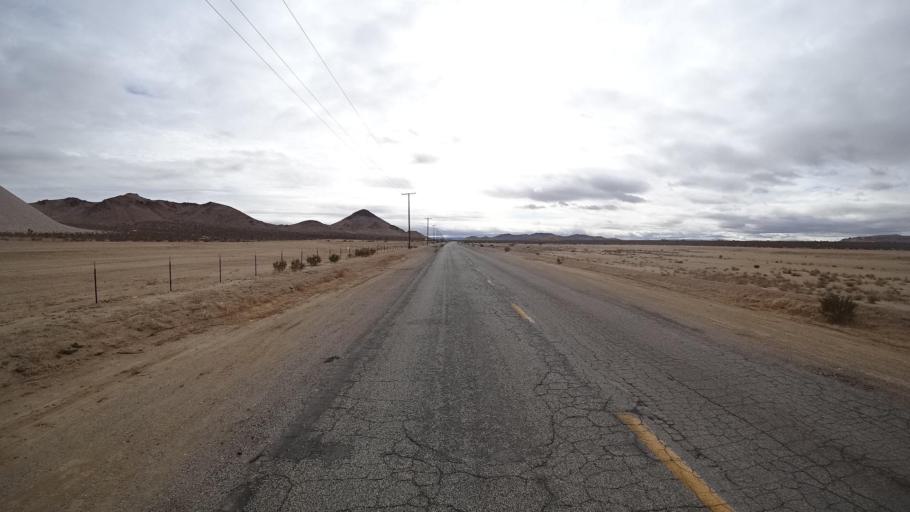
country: US
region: California
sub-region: Kern County
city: Mojave
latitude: 34.9821
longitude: -118.2089
